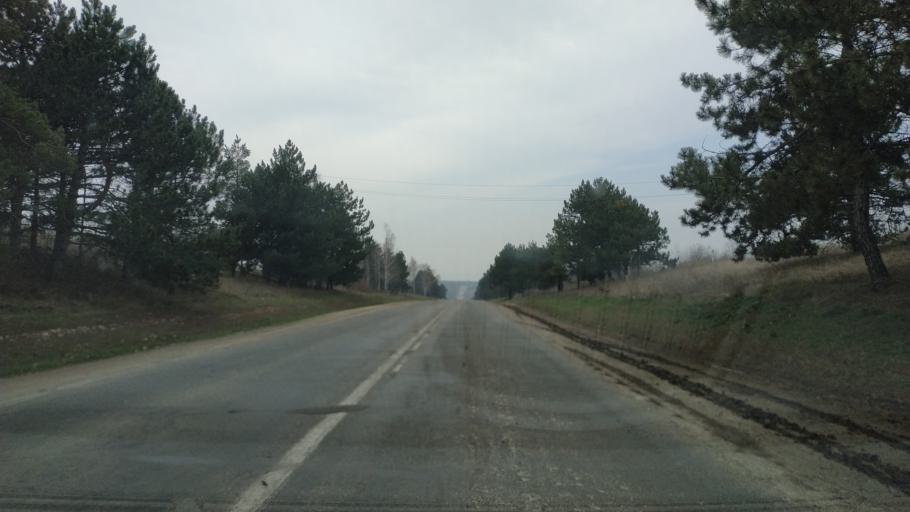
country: MD
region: Cahul
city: Cahul
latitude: 45.9322
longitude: 28.2753
